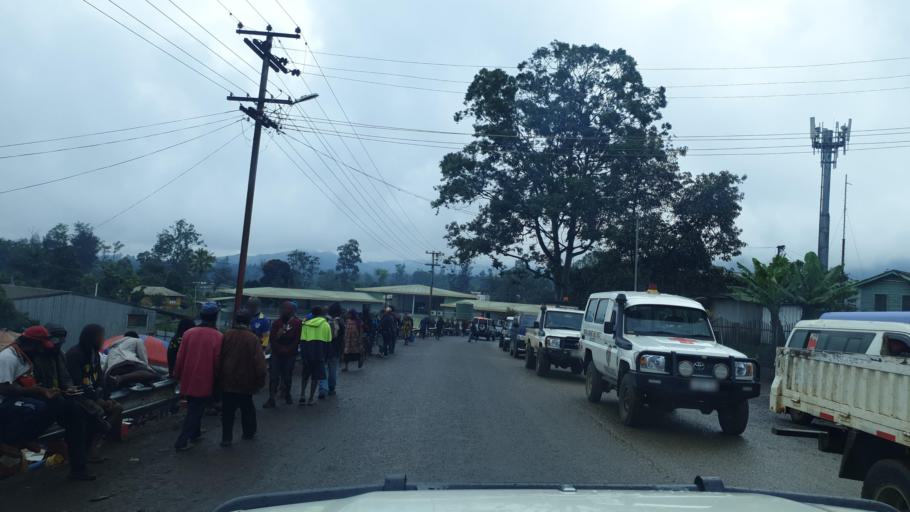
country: PG
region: Eastern Highlands
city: Goroka
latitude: -6.0731
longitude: 145.3889
